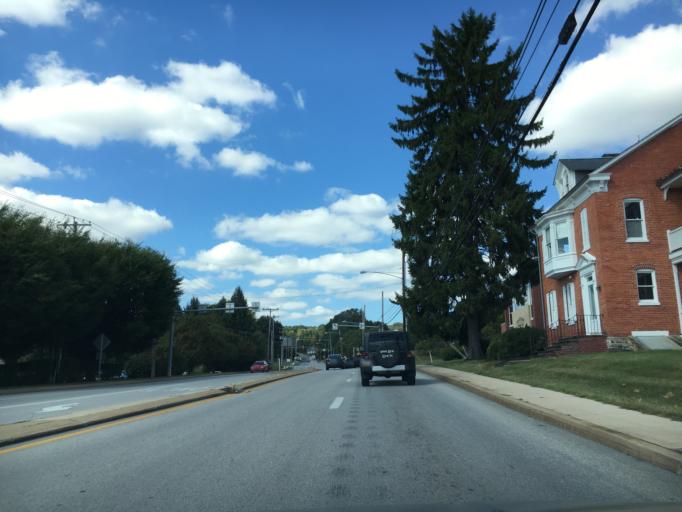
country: US
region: Pennsylvania
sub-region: York County
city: East York
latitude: 39.9913
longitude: -76.6709
